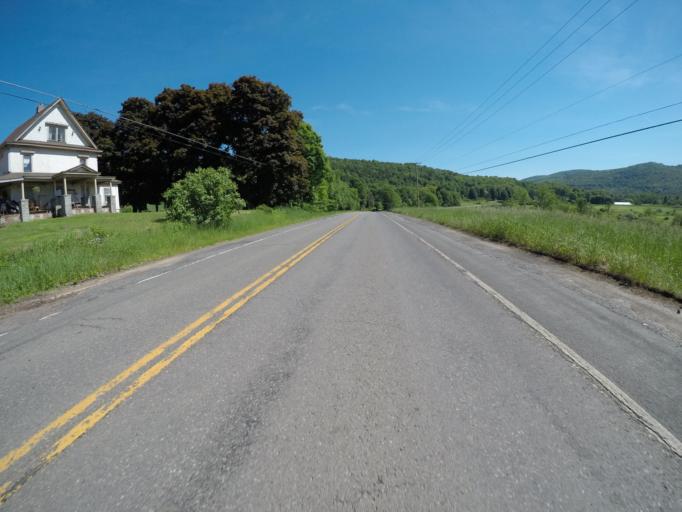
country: US
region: New York
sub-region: Delaware County
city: Delhi
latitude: 42.2121
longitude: -74.9786
